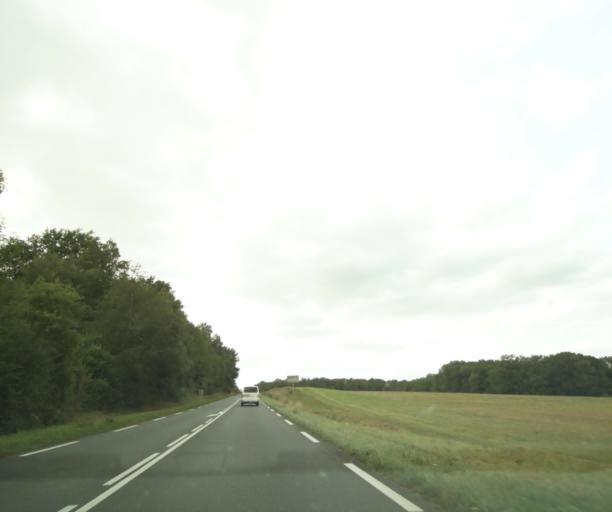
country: FR
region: Centre
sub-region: Departement d'Indre-et-Loire
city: Chambourg-sur-Indre
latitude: 47.1728
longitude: 0.9759
